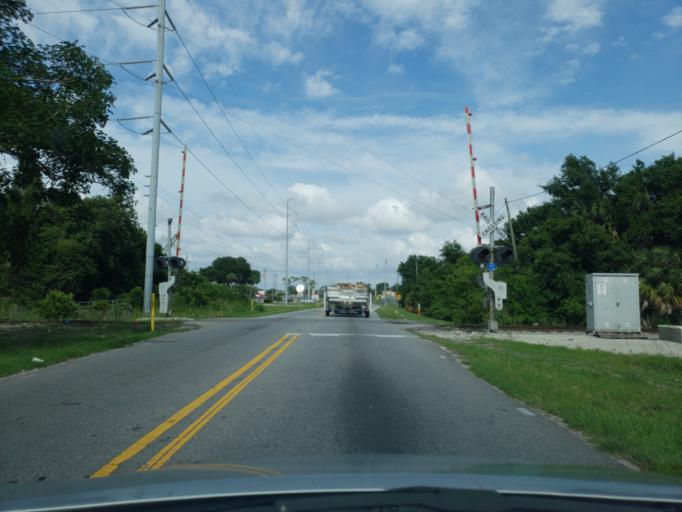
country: US
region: Florida
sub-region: Hillsborough County
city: Egypt Lake-Leto
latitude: 28.0109
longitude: -82.5260
